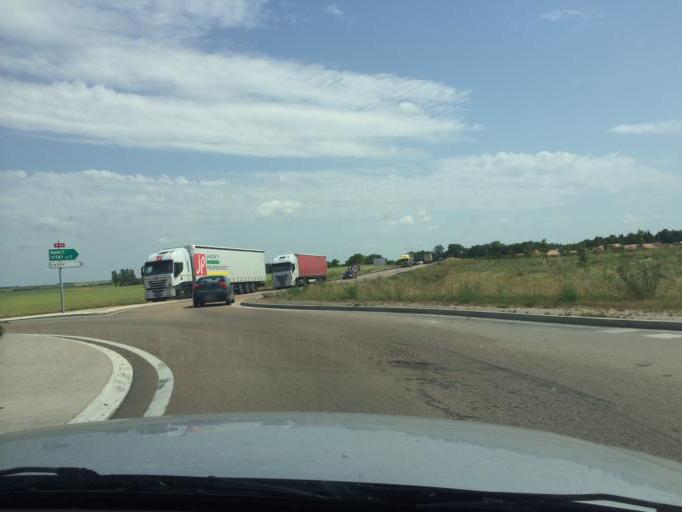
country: FR
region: Champagne-Ardenne
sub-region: Departement de la Marne
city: Sarry
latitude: 48.9107
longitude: 4.4305
